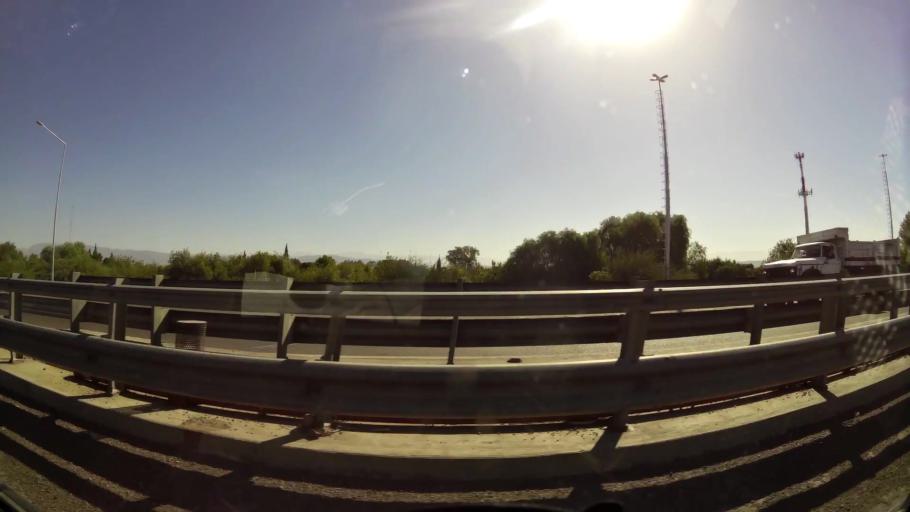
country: AR
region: San Juan
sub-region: Departamento de Santa Lucia
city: Santa Lucia
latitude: -31.5361
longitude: -68.5039
